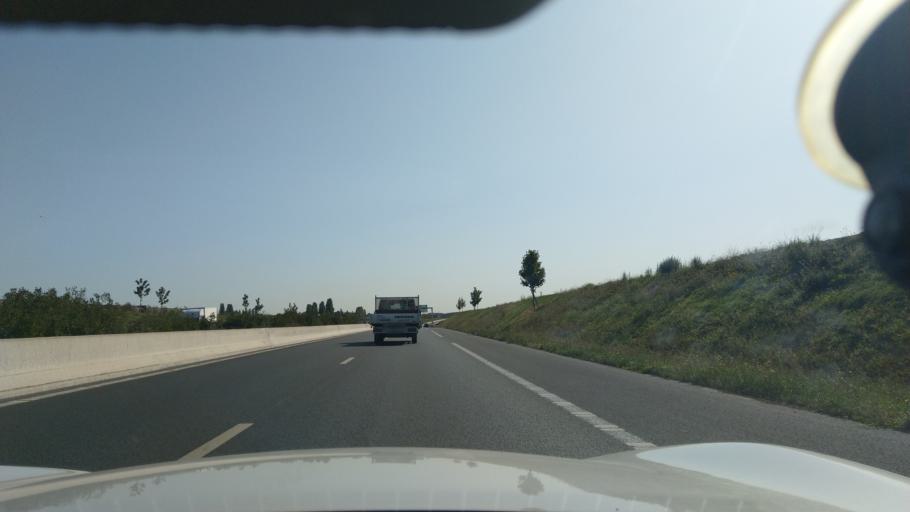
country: FR
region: Ile-de-France
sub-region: Departement du Val-d'Oise
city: Gonesse
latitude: 48.9779
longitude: 2.4447
